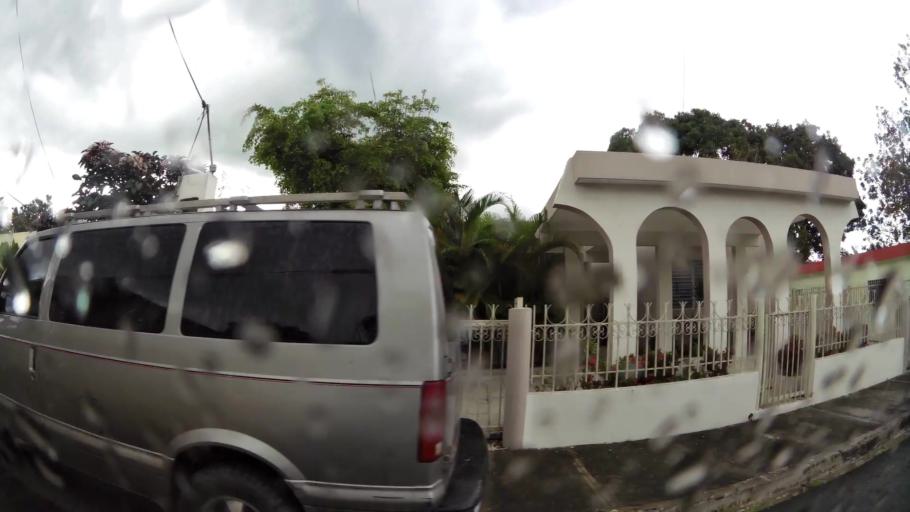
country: DO
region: Monsenor Nouel
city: Bonao
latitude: 18.9496
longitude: -70.4055
